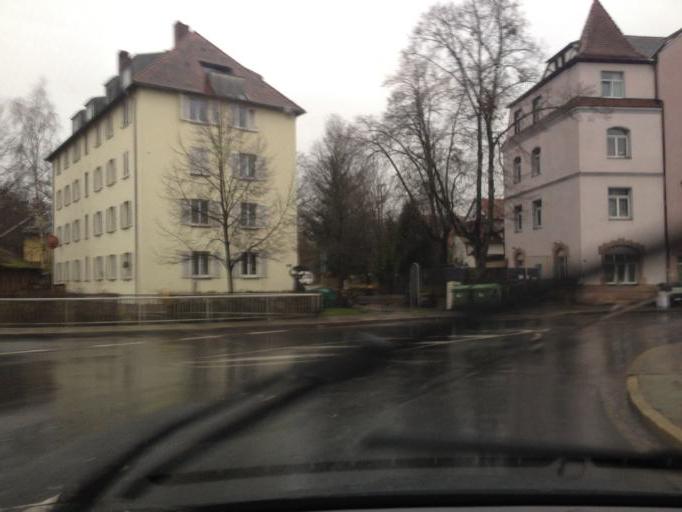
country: DE
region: Bavaria
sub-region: Regierungsbezirk Mittelfranken
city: Rothenbach an der Pegnitz
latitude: 49.4820
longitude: 11.2387
